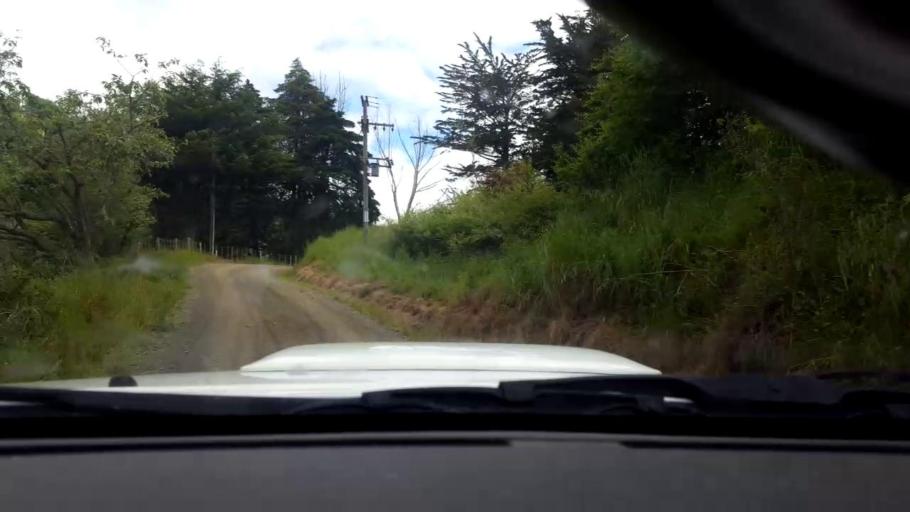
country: NZ
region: Gisborne
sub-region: Gisborne District
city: Gisborne
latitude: -38.4880
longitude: 177.6868
